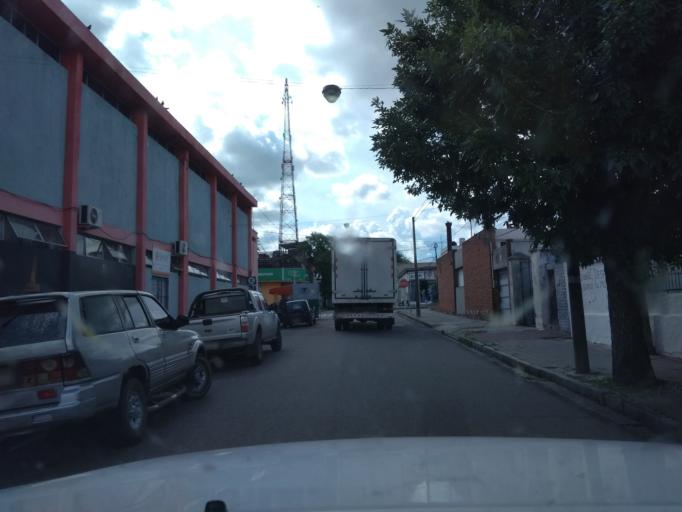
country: UY
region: Florida
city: Florida
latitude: -34.1006
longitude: -56.2112
